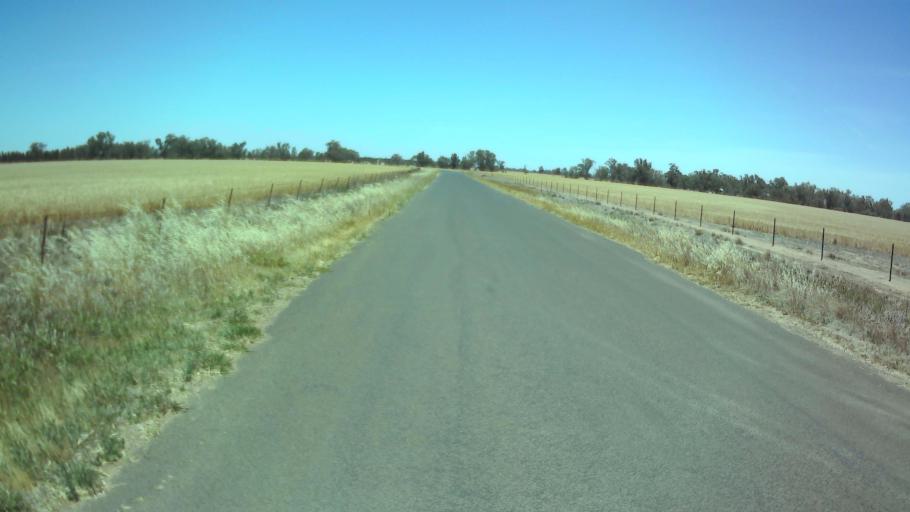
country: AU
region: New South Wales
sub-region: Weddin
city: Grenfell
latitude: -34.0330
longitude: 147.7902
